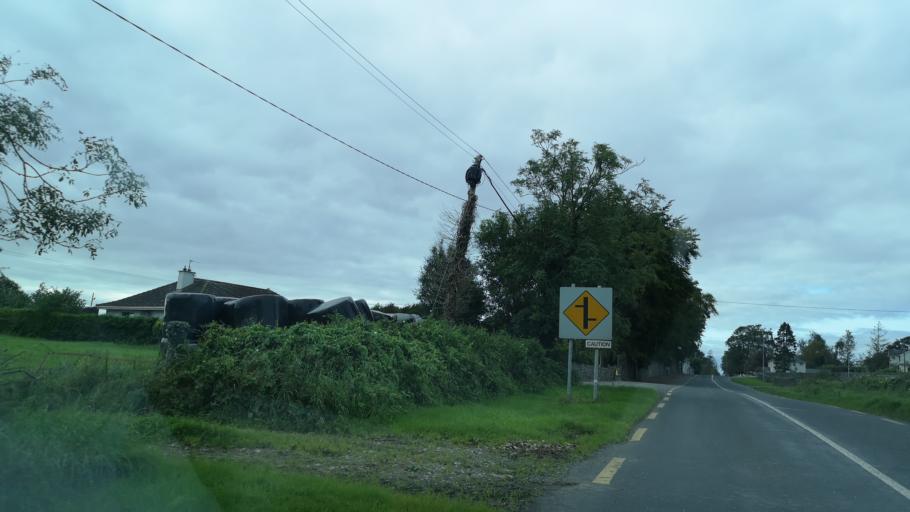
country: IE
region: Leinster
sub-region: Uibh Fhaili
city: Banagher
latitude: 53.2422
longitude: -7.9352
